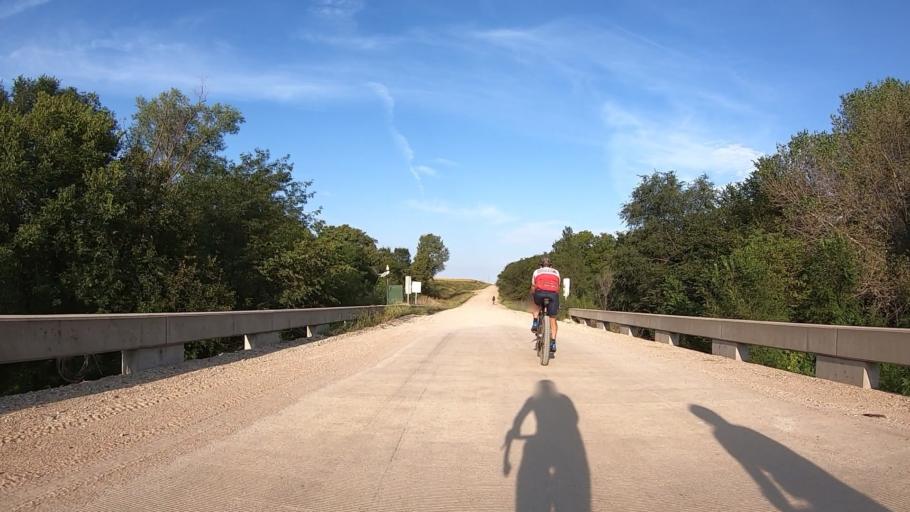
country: US
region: Kansas
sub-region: Marshall County
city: Blue Rapids
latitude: 39.7258
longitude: -96.8050
